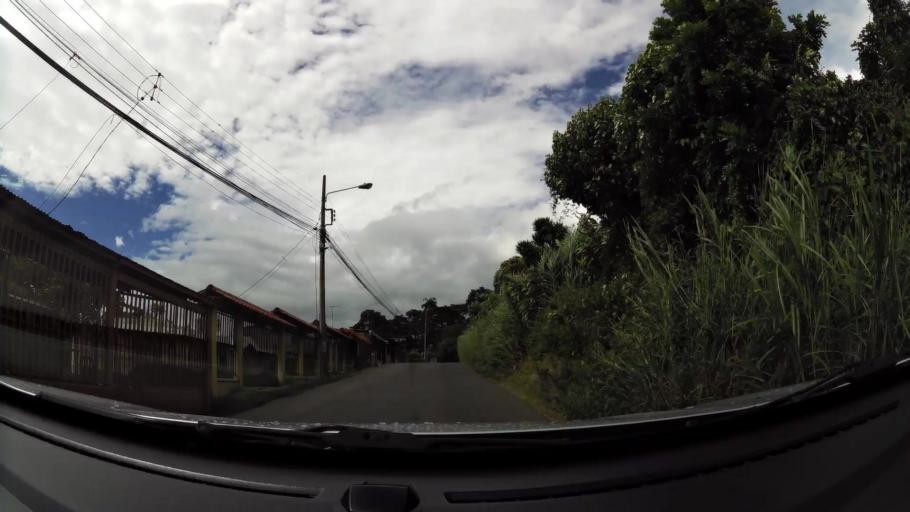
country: CR
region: Cartago
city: Tres Rios
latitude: 9.9112
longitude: -83.9874
